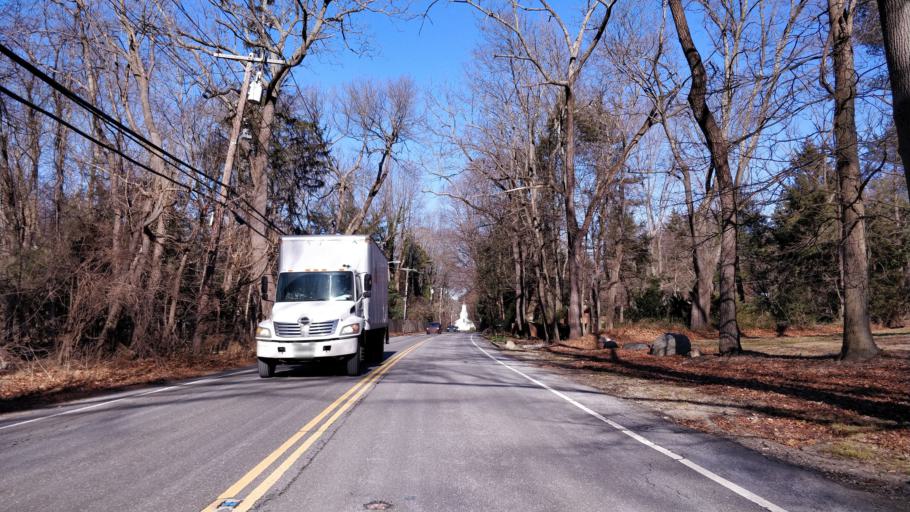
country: US
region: New York
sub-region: Nassau County
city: Brookville
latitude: 40.8248
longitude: -73.5709
